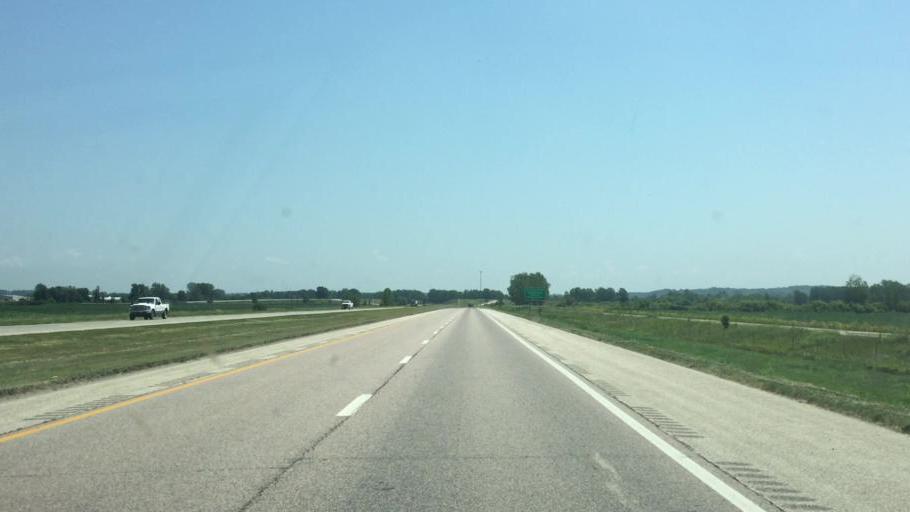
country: US
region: Kansas
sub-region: Doniphan County
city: Elwood
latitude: 39.7404
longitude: -94.9075
